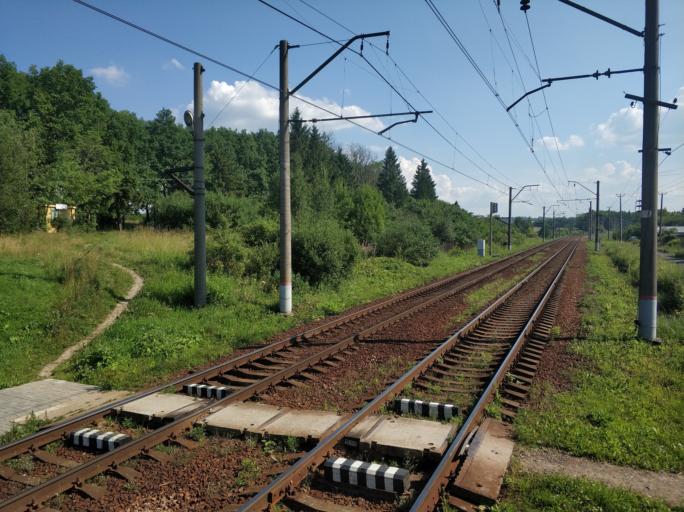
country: RU
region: St.-Petersburg
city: Gorelovo
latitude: 59.7508
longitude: 30.1168
